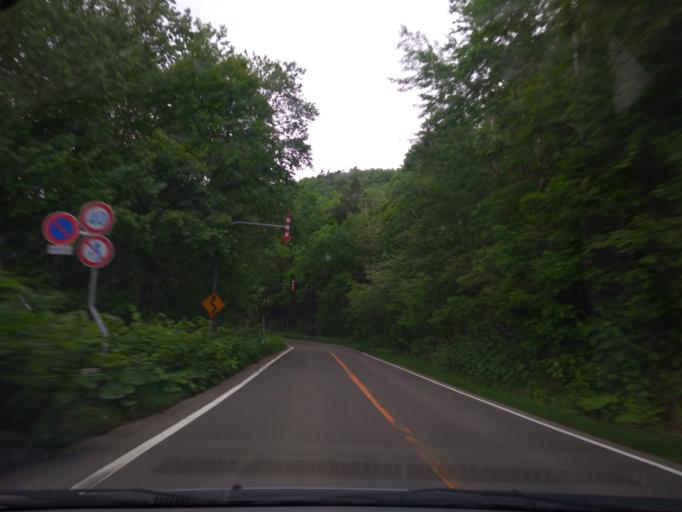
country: JP
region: Hokkaido
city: Shimo-furano
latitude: 43.1374
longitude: 142.4610
